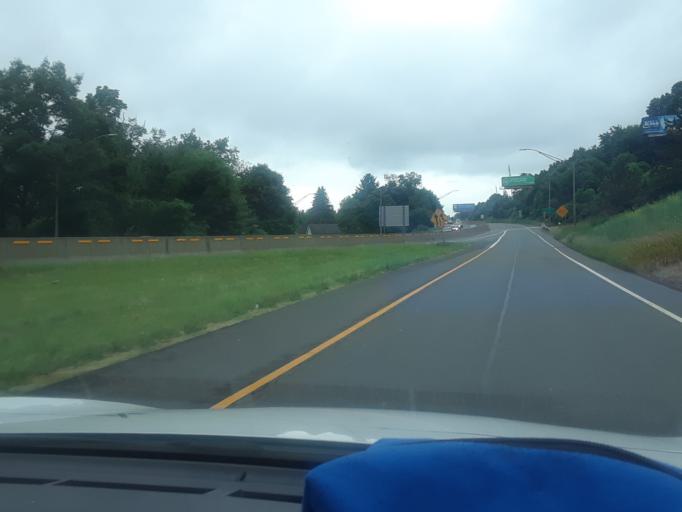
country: US
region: Pennsylvania
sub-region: Lackawanna County
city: Chinchilla
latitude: 41.4531
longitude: -75.6655
